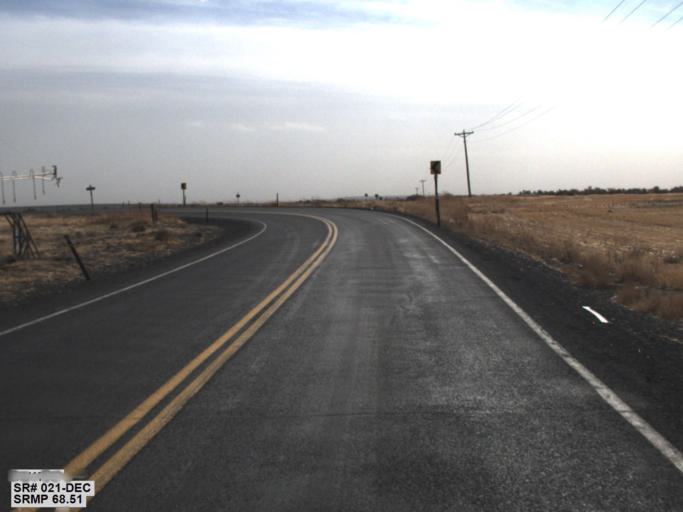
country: US
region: Washington
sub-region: Okanogan County
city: Coulee Dam
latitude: 47.4741
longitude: -118.7847
